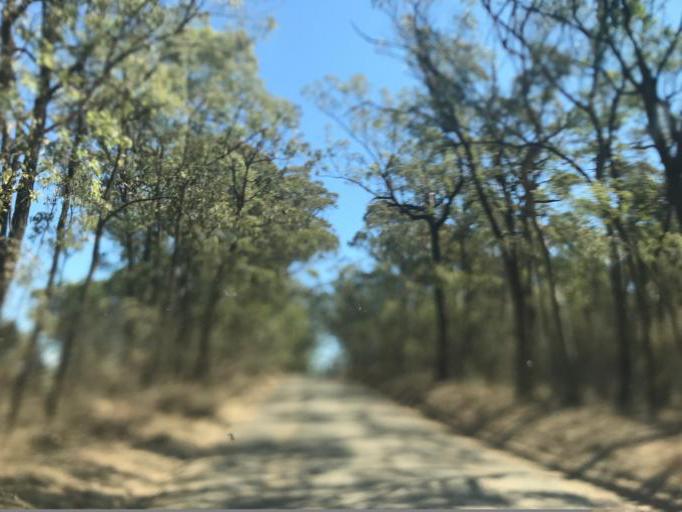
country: AU
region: New South Wales
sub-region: Hawkesbury
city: Pitt Town
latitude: -33.4640
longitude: 150.8449
